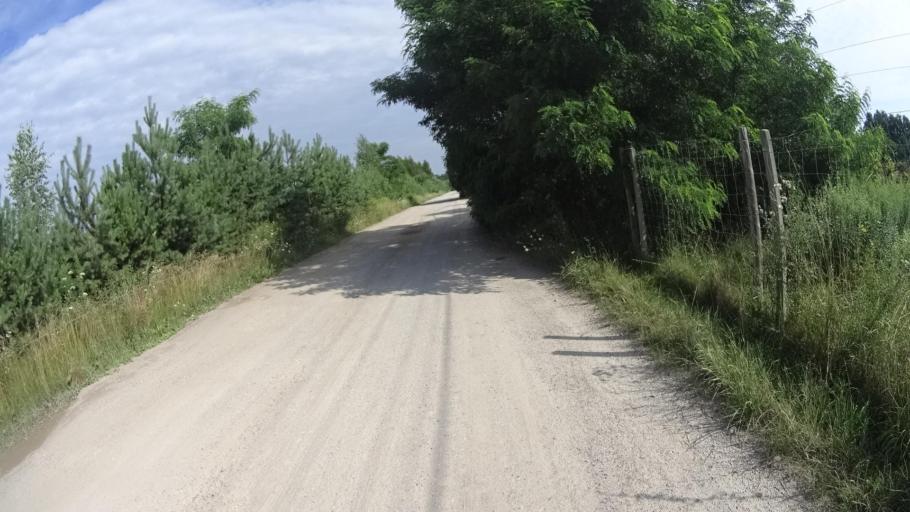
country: PL
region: Masovian Voivodeship
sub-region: Powiat piaseczynski
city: Tarczyn
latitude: 51.9727
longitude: 20.8539
